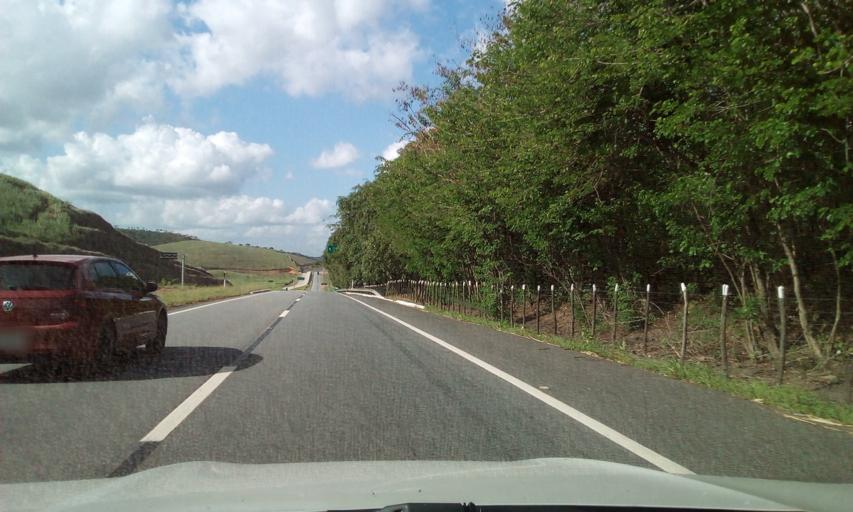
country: BR
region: Alagoas
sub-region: Novo Lino
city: Novo Lino
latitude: -8.8719
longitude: -35.6296
